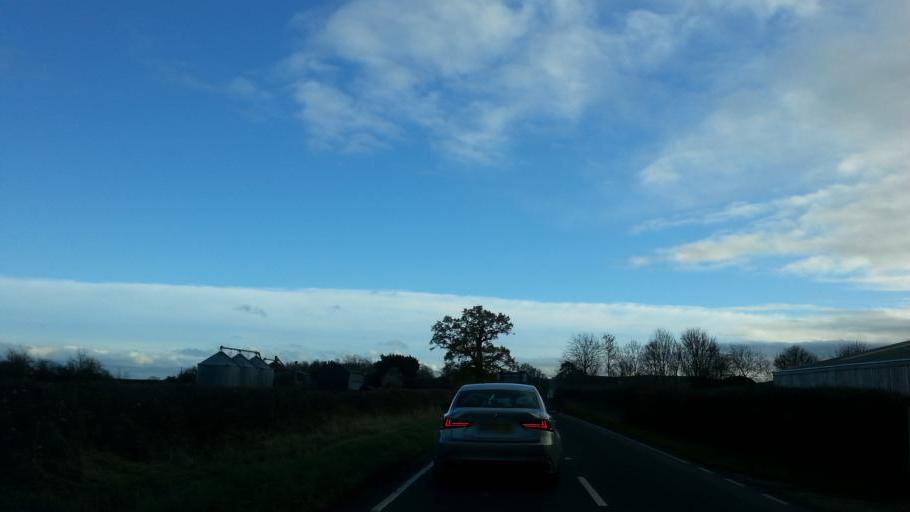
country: GB
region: England
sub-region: Oxfordshire
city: Shrivenham
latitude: 51.6125
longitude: -1.6147
